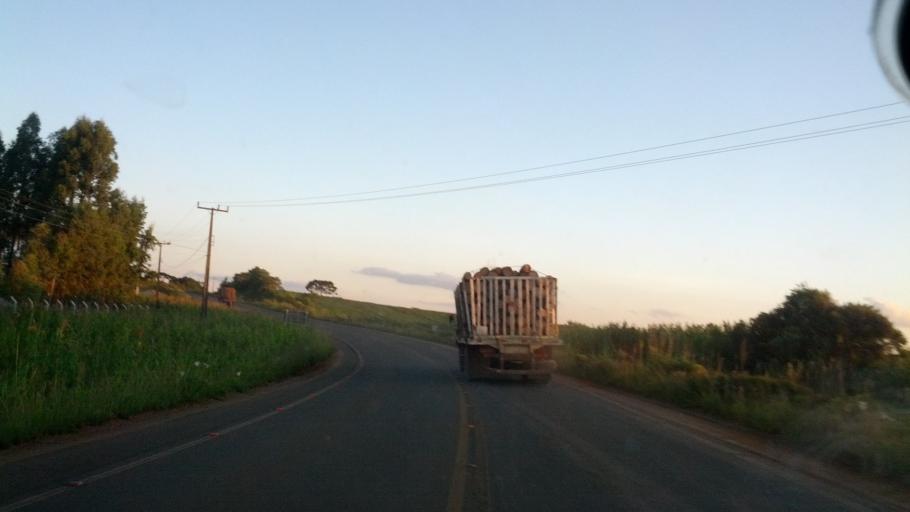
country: BR
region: Rio Grande do Sul
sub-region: Vacaria
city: Estrela
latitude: -27.8025
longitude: -50.8632
